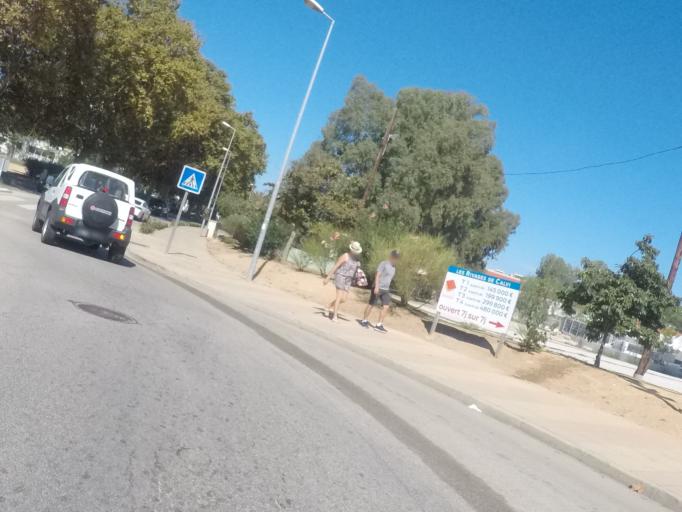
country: FR
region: Corsica
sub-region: Departement de la Haute-Corse
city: Calvi
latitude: 42.5538
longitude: 8.7630
